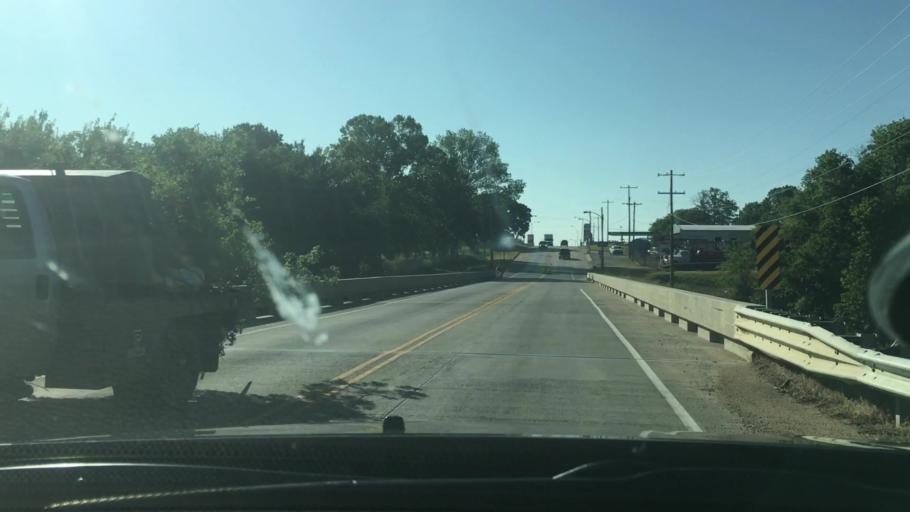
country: US
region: Oklahoma
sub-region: Johnston County
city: Tishomingo
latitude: 34.2394
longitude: -96.6856
